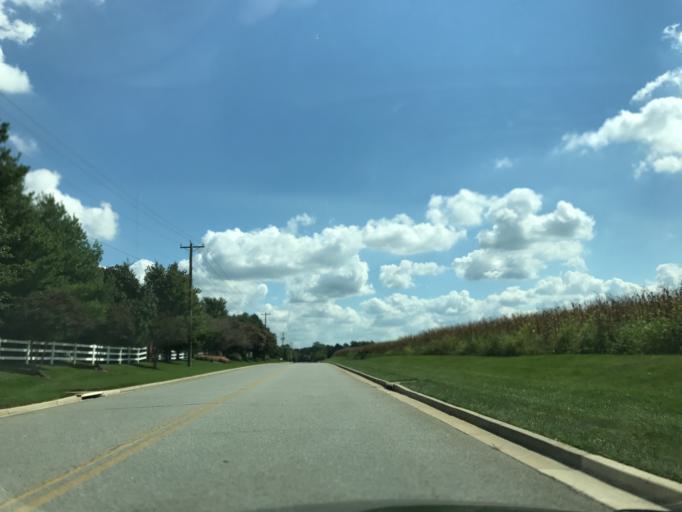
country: US
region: Maryland
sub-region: Queen Anne's County
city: Centreville
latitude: 39.0232
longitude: -76.0741
